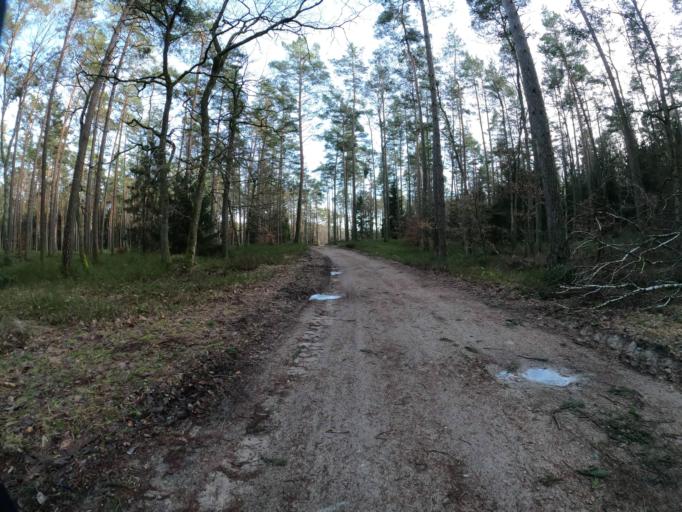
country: PL
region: West Pomeranian Voivodeship
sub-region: Powiat koszalinski
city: Polanow
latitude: 54.1722
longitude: 16.6590
